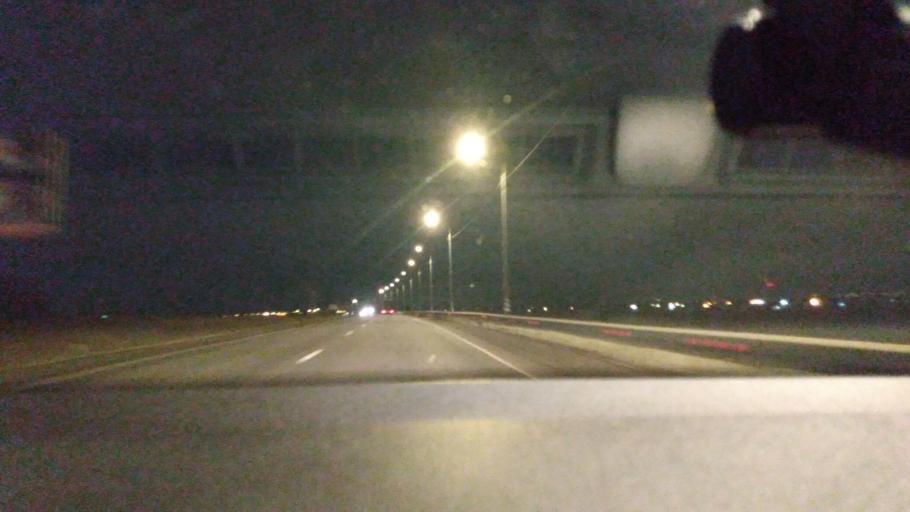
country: RU
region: Moskovskaya
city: Yegor'yevsk
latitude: 55.3997
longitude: 39.0613
